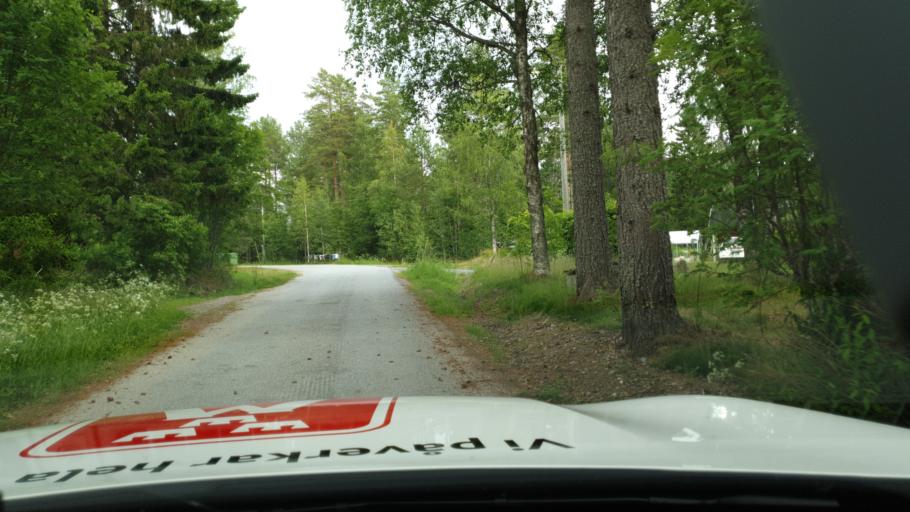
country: SE
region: Vaesterbotten
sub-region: Umea Kommun
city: Hoernefors
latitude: 63.5441
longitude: 19.7745
